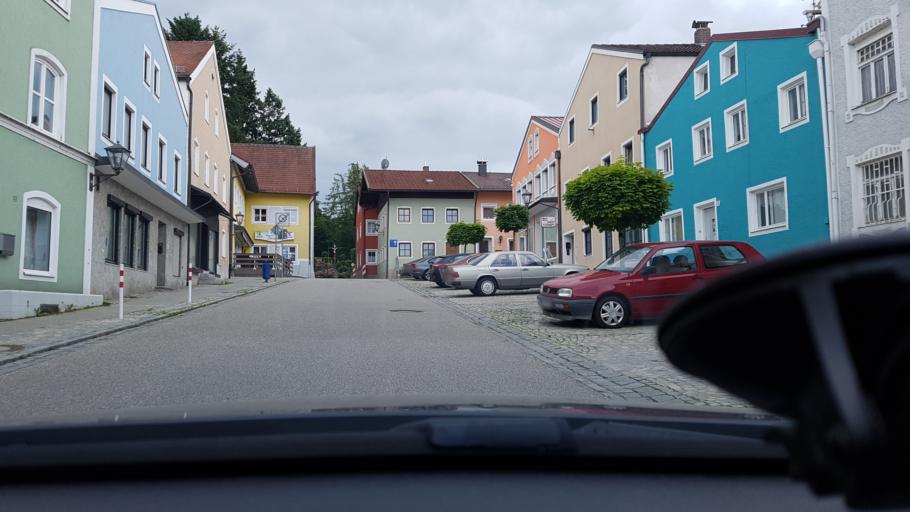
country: DE
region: Bavaria
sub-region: Lower Bavaria
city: Triftern
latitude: 48.3944
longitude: 13.0045
